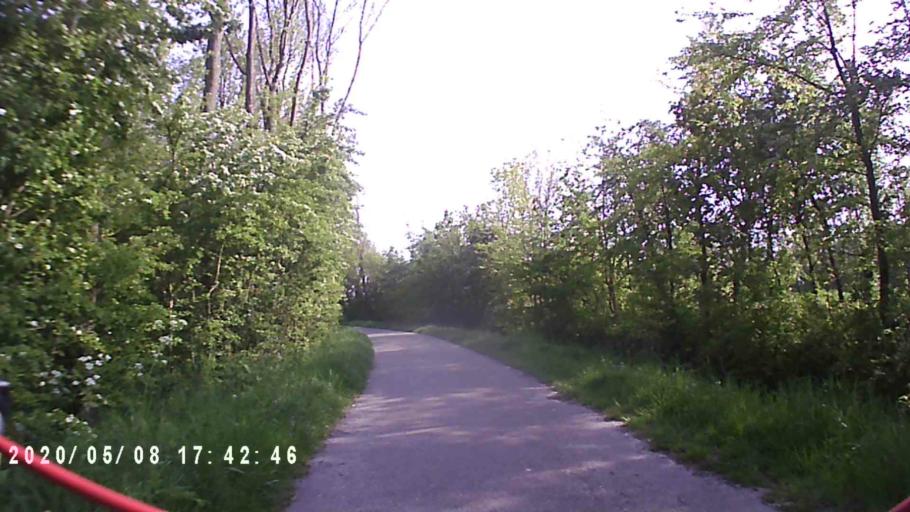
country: NL
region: Groningen
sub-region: Gemeente Winsum
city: Winsum
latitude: 53.3682
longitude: 6.5200
